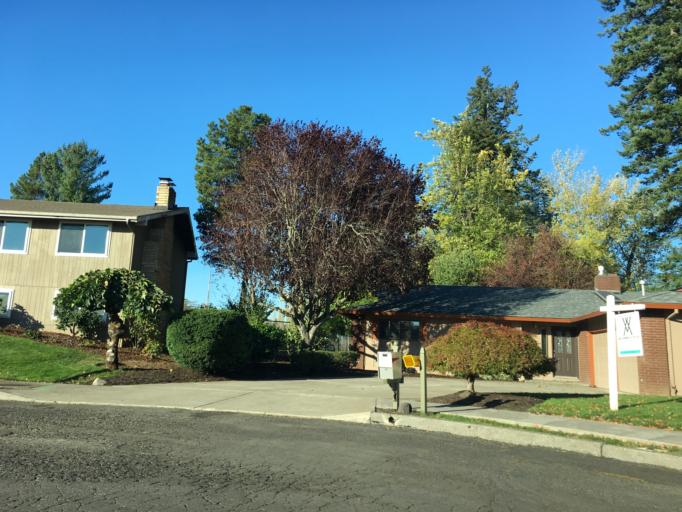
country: US
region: Oregon
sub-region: Multnomah County
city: Gresham
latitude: 45.5087
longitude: -122.4087
